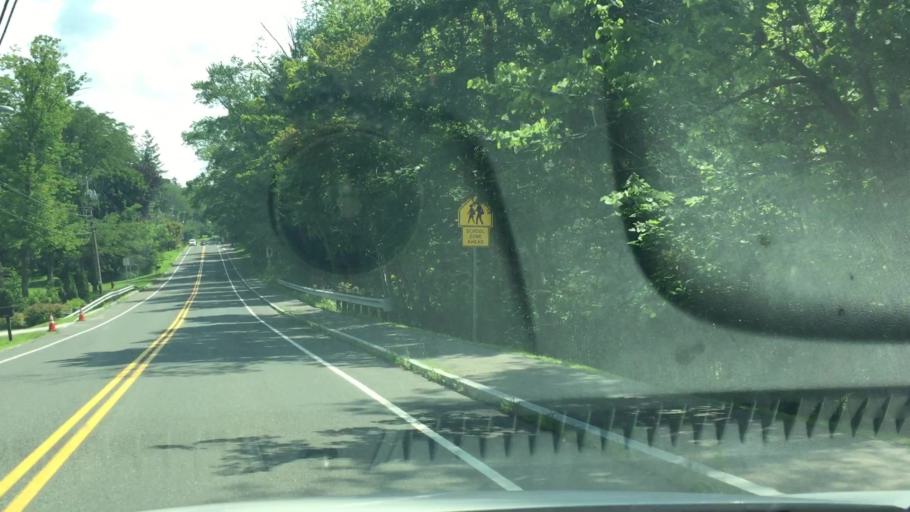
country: US
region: Massachusetts
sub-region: Berkshire County
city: Lenox
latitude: 42.3560
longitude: -73.2993
